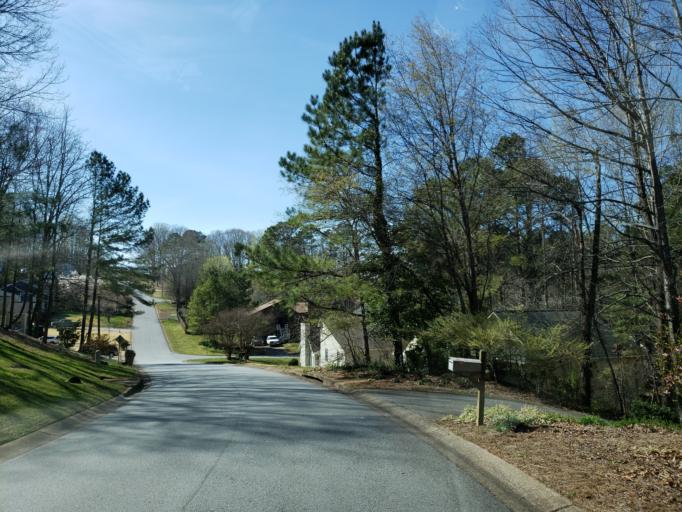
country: US
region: Georgia
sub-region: Cherokee County
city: Woodstock
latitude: 34.0363
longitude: -84.4894
